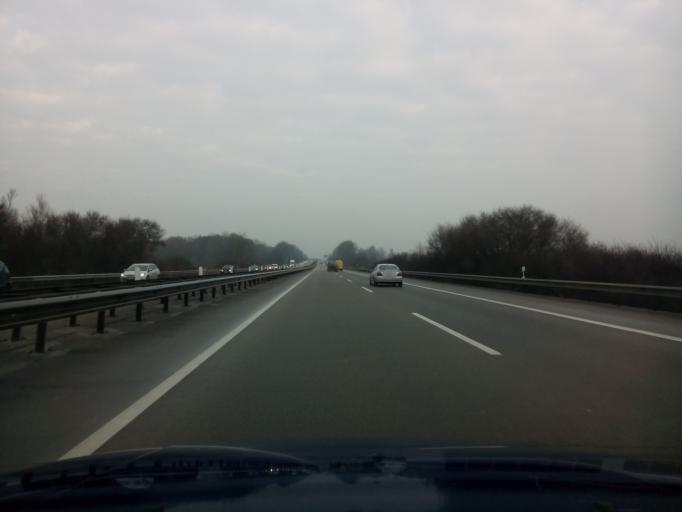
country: DE
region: Lower Saxony
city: Schiffdorf
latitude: 53.5632
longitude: 8.6196
